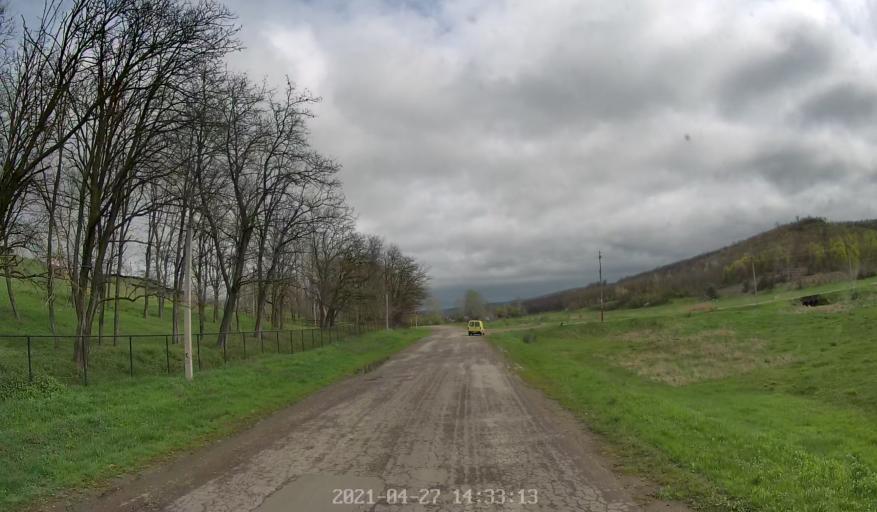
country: MD
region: Chisinau
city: Vadul lui Voda
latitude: 47.0605
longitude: 29.0184
